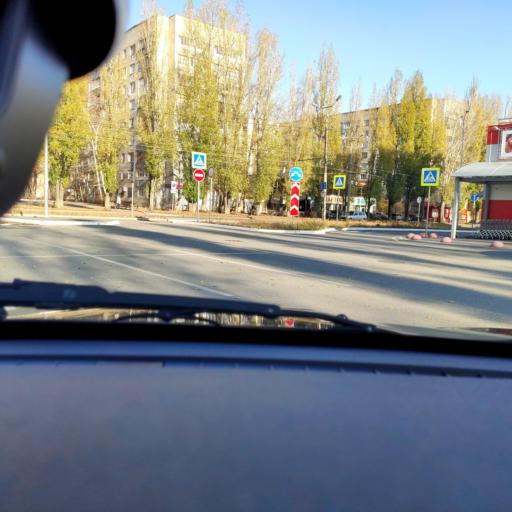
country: RU
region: Samara
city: Tol'yatti
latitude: 53.5087
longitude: 49.4238
